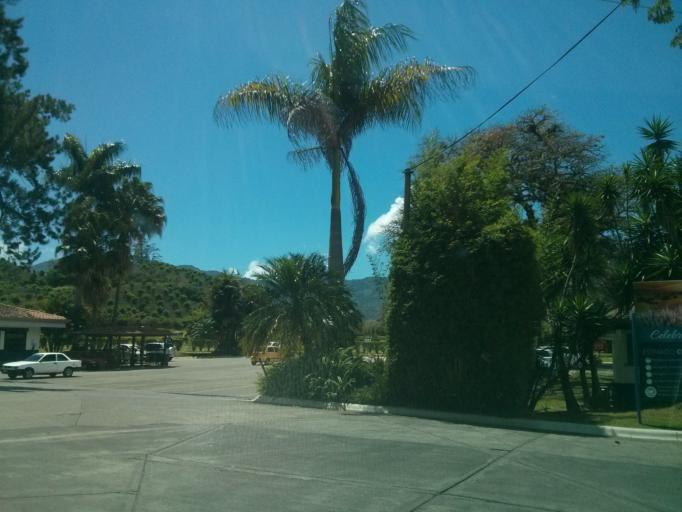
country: CR
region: San Jose
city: San Miguel
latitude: 9.8825
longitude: -84.0610
